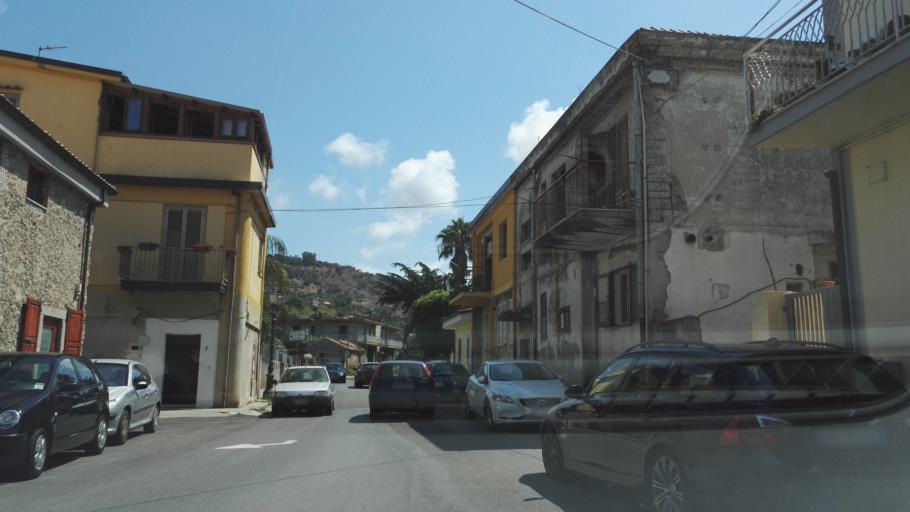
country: IT
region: Calabria
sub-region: Provincia di Vibo-Valentia
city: Nicotera
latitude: 38.5463
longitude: 15.9354
